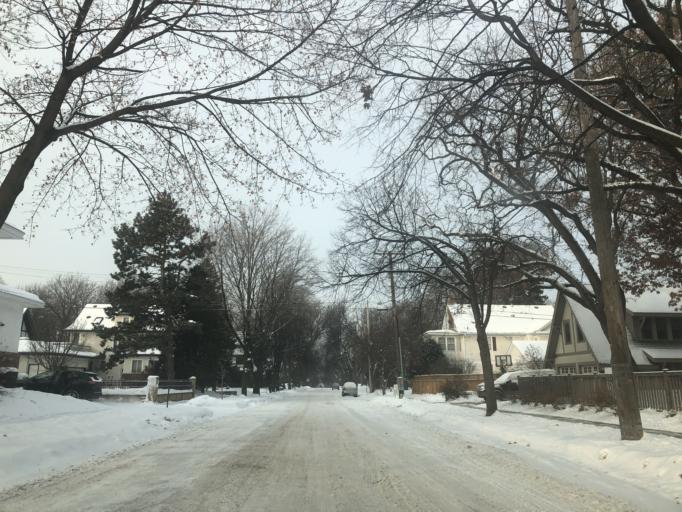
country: US
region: Minnesota
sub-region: Hennepin County
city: Richfield
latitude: 44.9178
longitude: -93.2935
